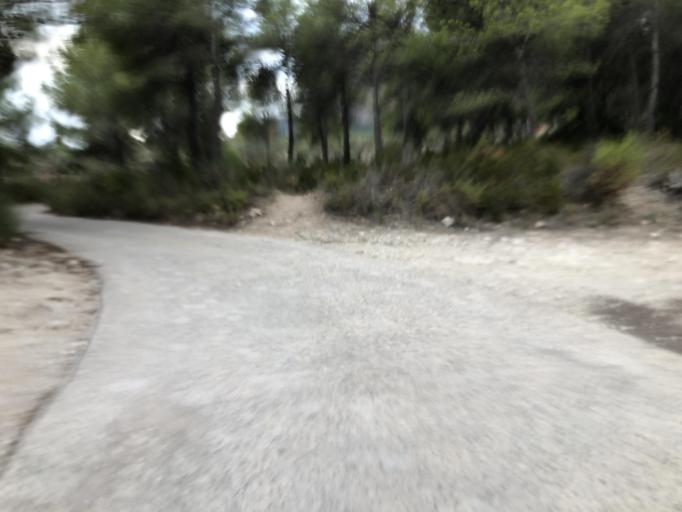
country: ES
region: Valencia
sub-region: Provincia de Alicante
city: Polop
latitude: 38.6372
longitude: -0.1416
